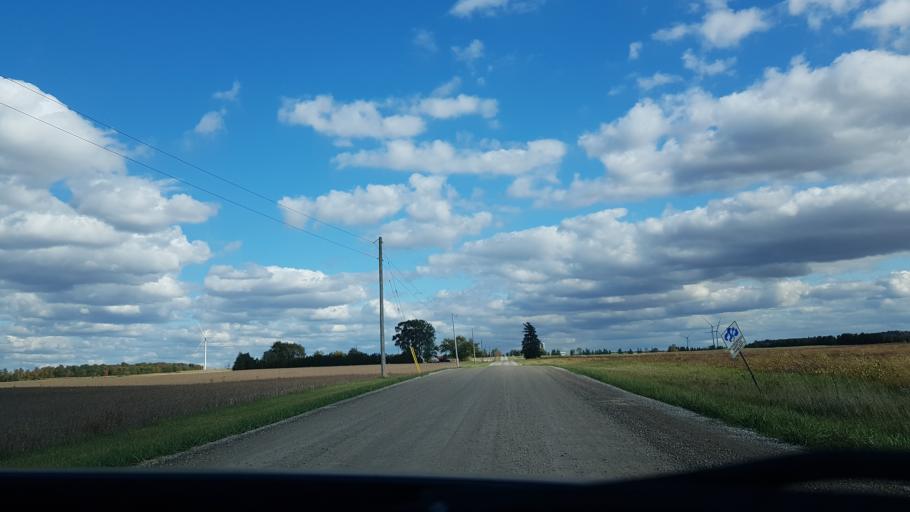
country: CA
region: Ontario
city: South Huron
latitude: 43.1166
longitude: -81.6719
